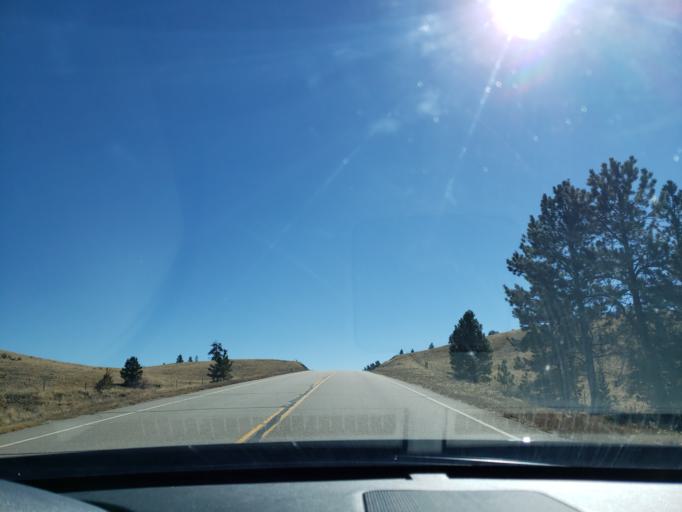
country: US
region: Colorado
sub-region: Chaffee County
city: Buena Vista
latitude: 38.8926
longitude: -105.6882
